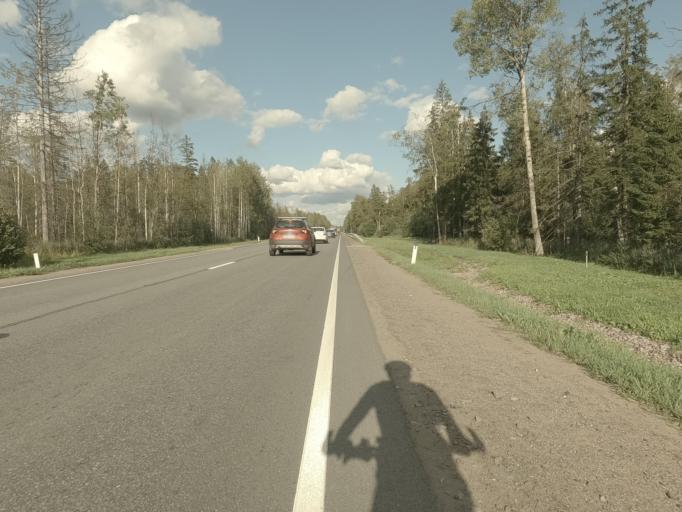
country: RU
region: Leningrad
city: Pavlovo
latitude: 59.6749
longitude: 30.9227
